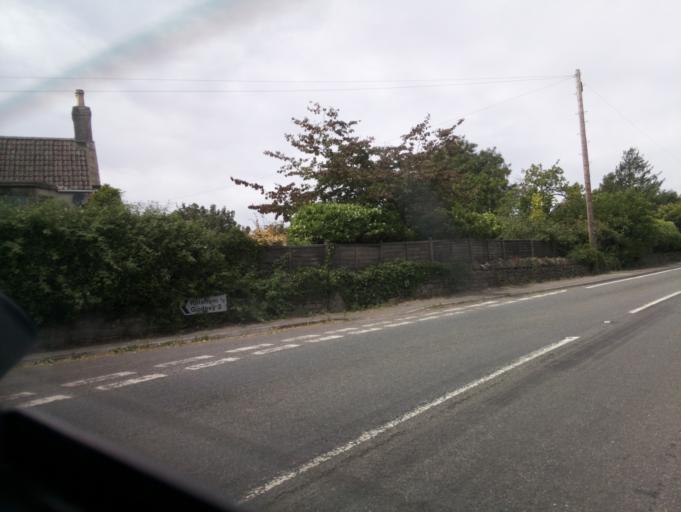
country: GB
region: England
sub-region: Somerset
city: Glastonbury
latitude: 51.1826
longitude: -2.6914
